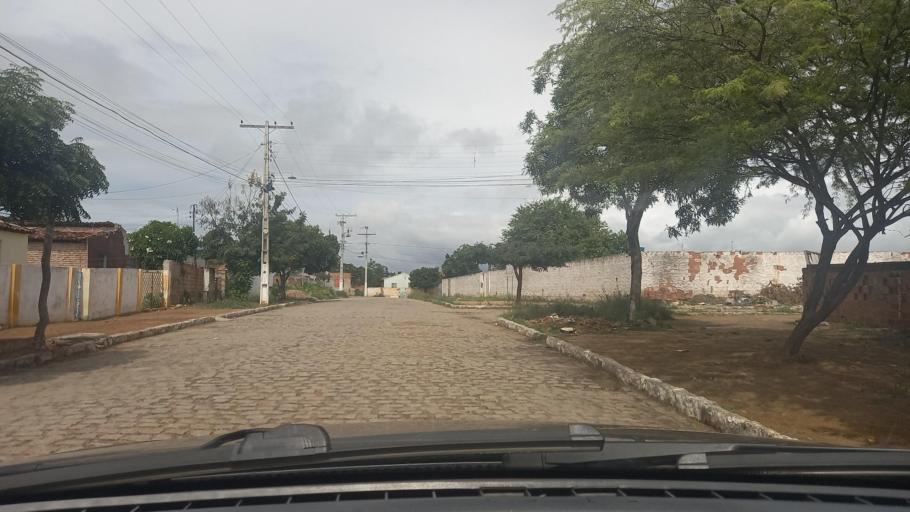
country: BR
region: Bahia
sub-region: Paulo Afonso
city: Paulo Afonso
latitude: -9.3457
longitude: -38.2600
